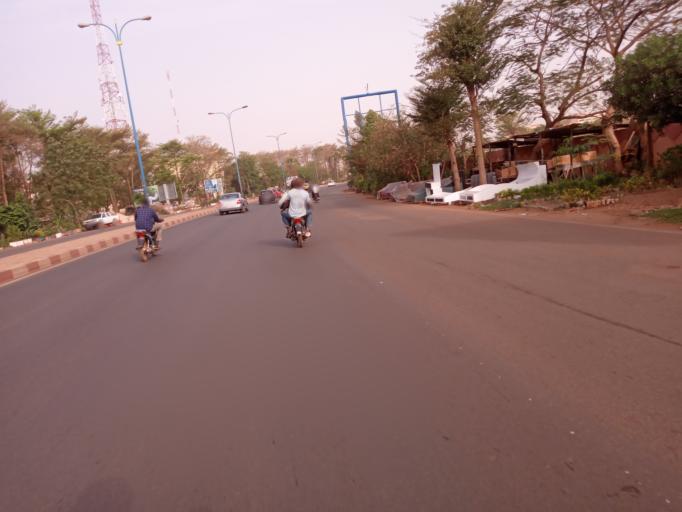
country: ML
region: Bamako
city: Bamako
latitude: 12.6385
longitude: -8.0189
